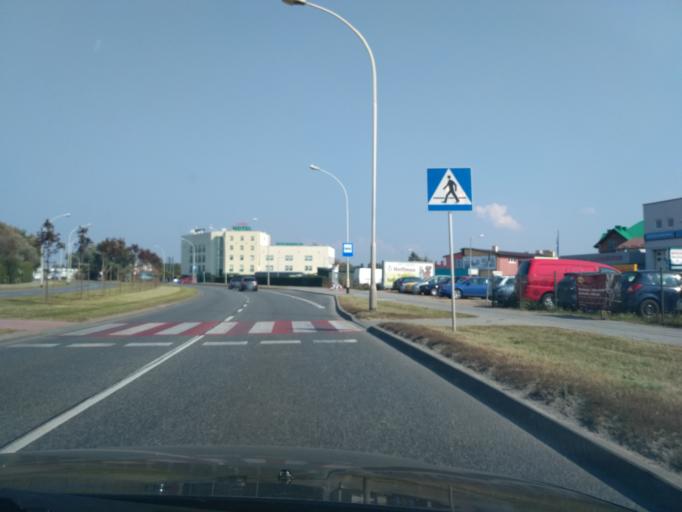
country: PL
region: Subcarpathian Voivodeship
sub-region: Rzeszow
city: Rzeszow
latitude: 50.0185
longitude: 22.0257
